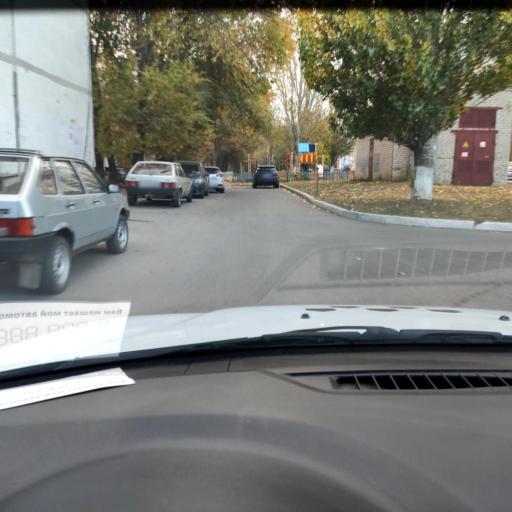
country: RU
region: Samara
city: Tol'yatti
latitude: 53.5096
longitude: 49.4324
